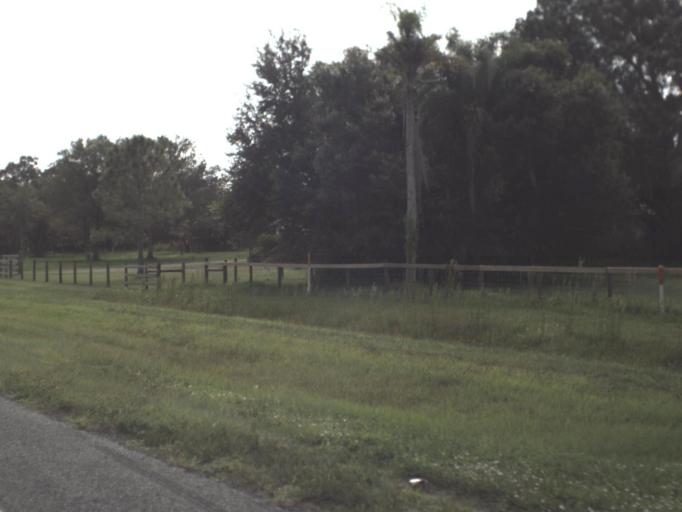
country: US
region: Florida
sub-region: Lee County
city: Alva
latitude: 26.7117
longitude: -81.6455
